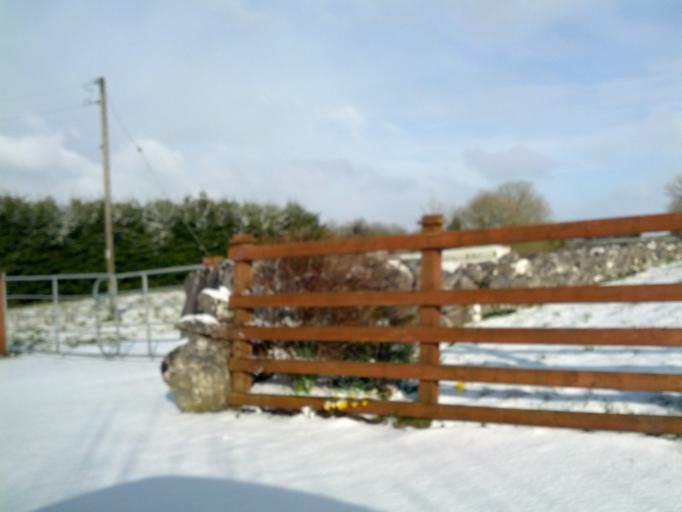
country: IE
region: Connaught
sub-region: County Galway
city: Athenry
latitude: 53.2187
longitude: -8.7629
